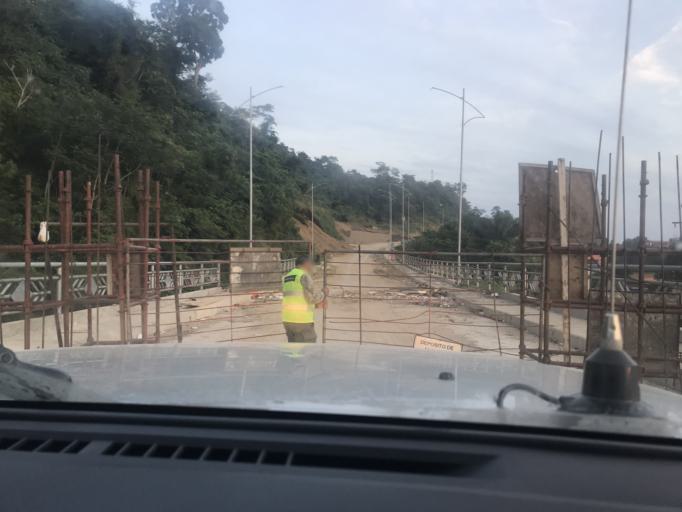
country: BO
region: El Beni
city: Rurrenabaque
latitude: -14.4424
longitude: -67.5351
